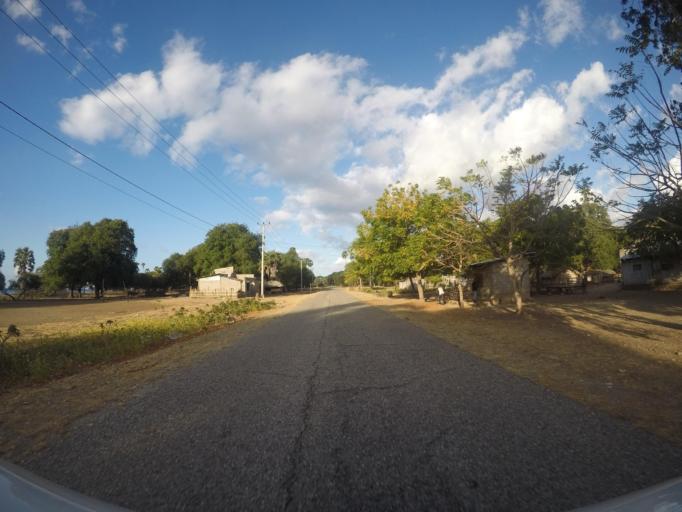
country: TL
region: Lautem
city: Lospalos
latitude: -8.3355
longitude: 126.9479
